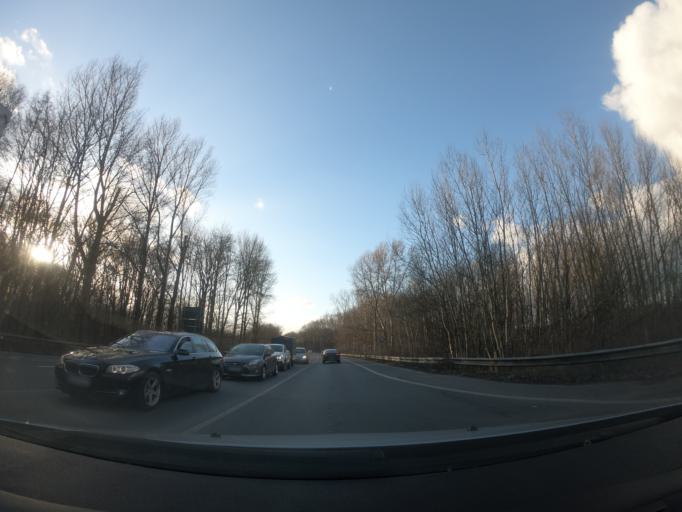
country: DE
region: North Rhine-Westphalia
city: Lunen
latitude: 51.6043
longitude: 7.4777
